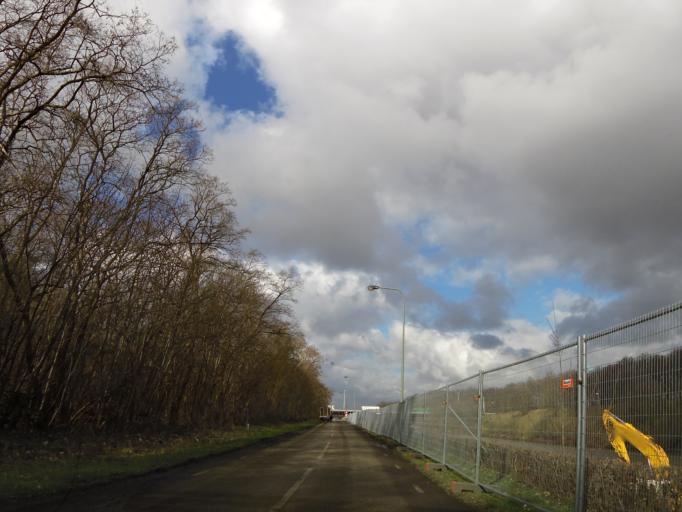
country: NL
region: Limburg
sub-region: Gemeente Stein
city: Elsloo
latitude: 50.9562
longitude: 5.7596
